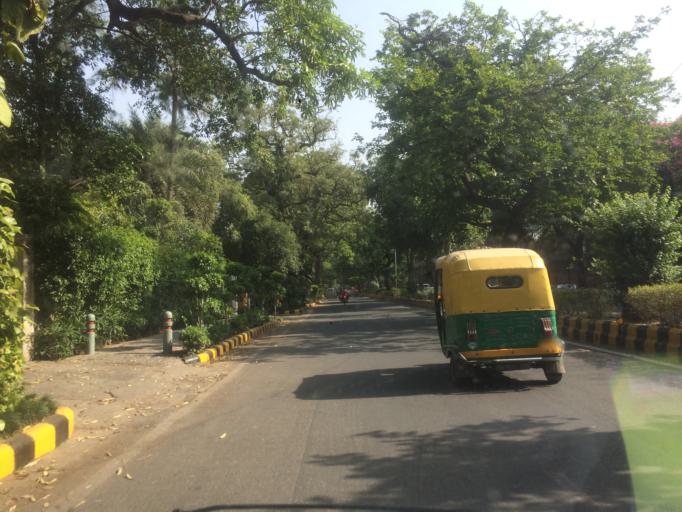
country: IN
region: NCT
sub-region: New Delhi
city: New Delhi
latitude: 28.5962
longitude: 77.2322
